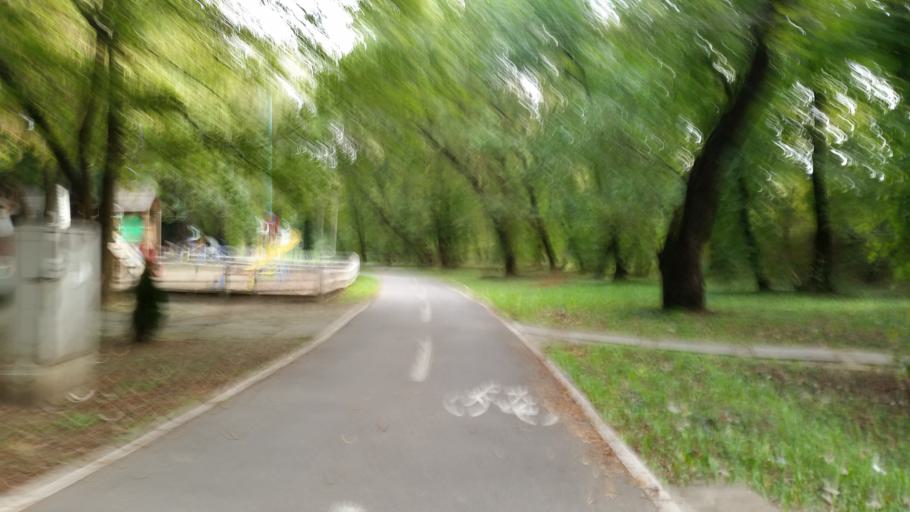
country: RS
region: Central Serbia
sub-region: Belgrade
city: Cukarica
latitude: 44.7796
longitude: 20.3828
